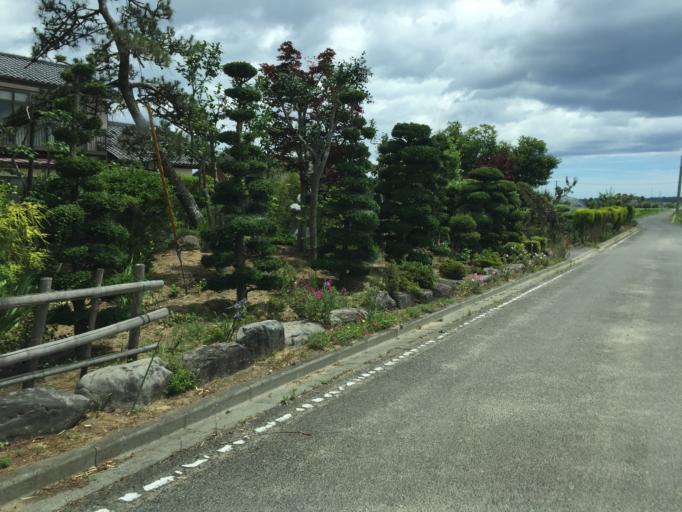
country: JP
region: Fukushima
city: Namie
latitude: 37.6501
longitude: 140.9716
